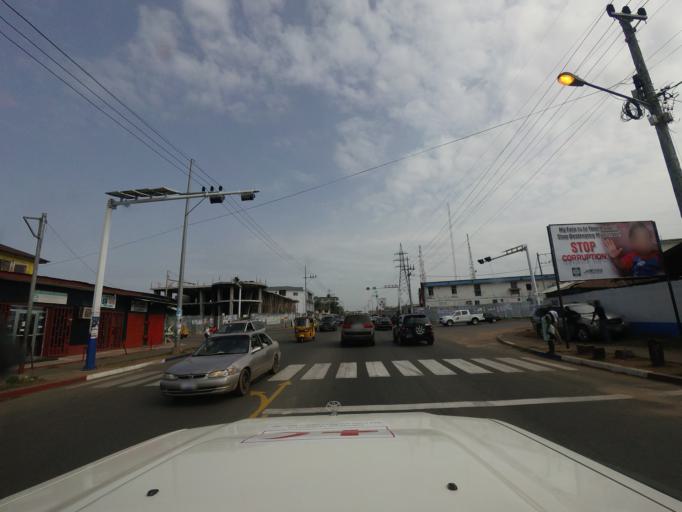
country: LR
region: Montserrado
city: Monrovia
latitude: 6.3057
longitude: -10.7966
